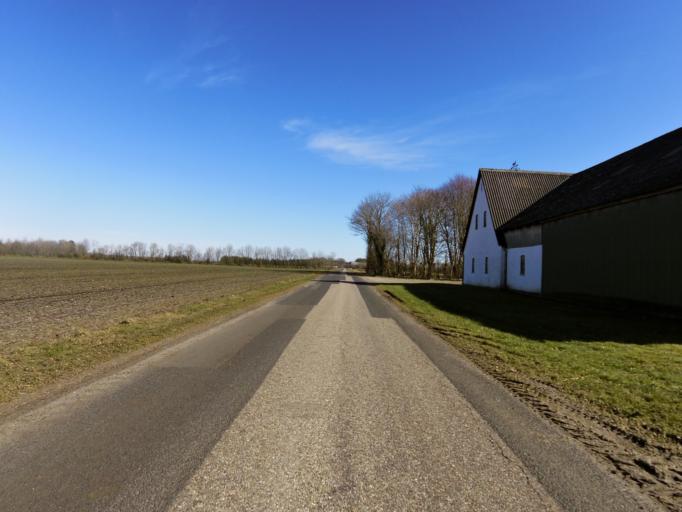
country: DK
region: South Denmark
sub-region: Tonder Kommune
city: Toftlund
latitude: 55.2372
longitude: 9.0933
